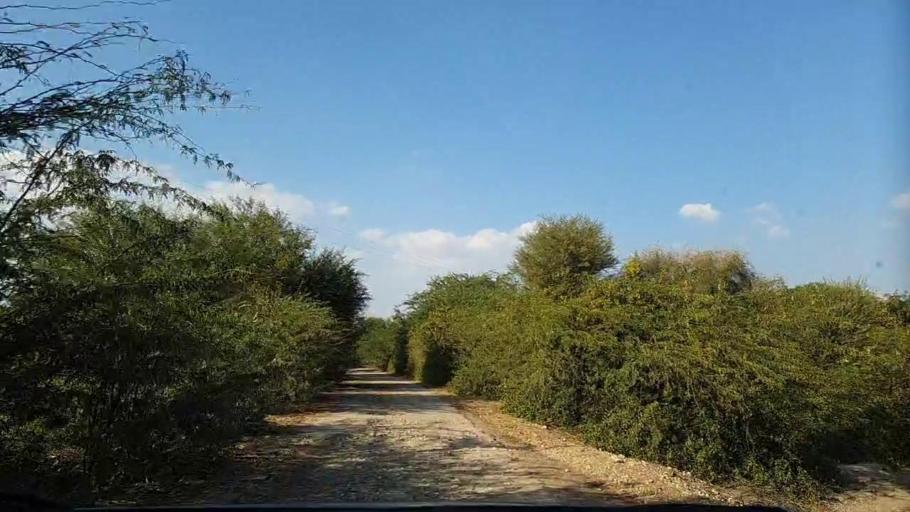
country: PK
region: Sindh
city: Pithoro
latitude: 25.6425
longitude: 69.3497
